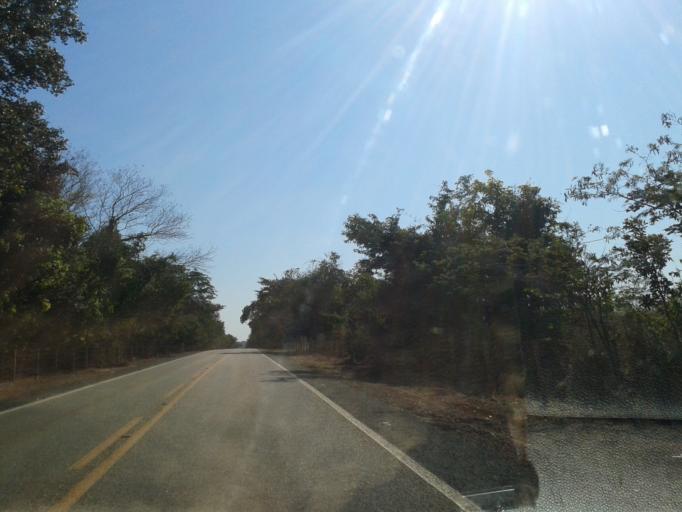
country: BR
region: Goias
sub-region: Mozarlandia
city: Mozarlandia
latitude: -14.6716
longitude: -50.5347
